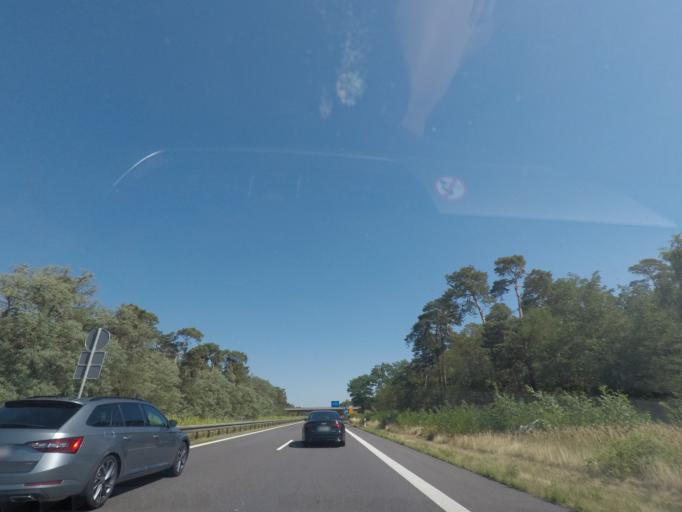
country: DE
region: Brandenburg
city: Calau
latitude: 51.7826
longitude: 13.8750
